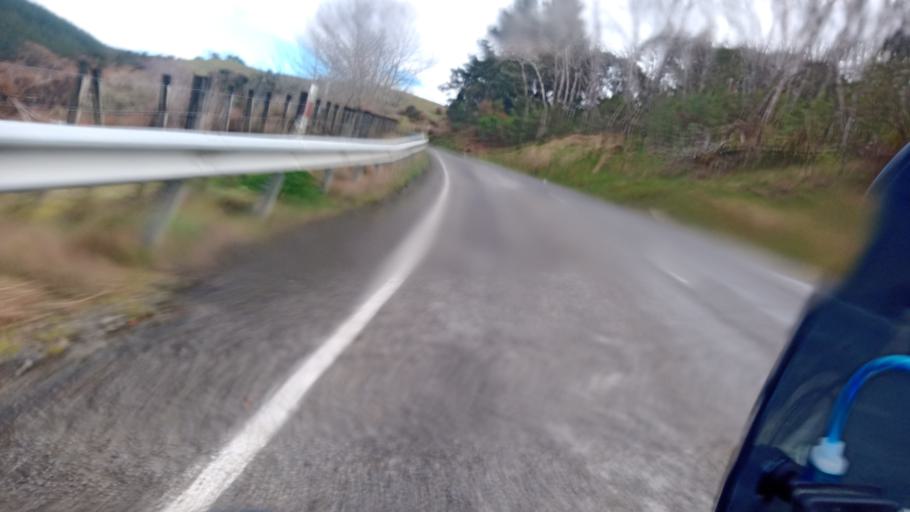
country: NZ
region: Gisborne
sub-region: Gisborne District
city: Gisborne
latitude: -38.0148
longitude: 178.2652
